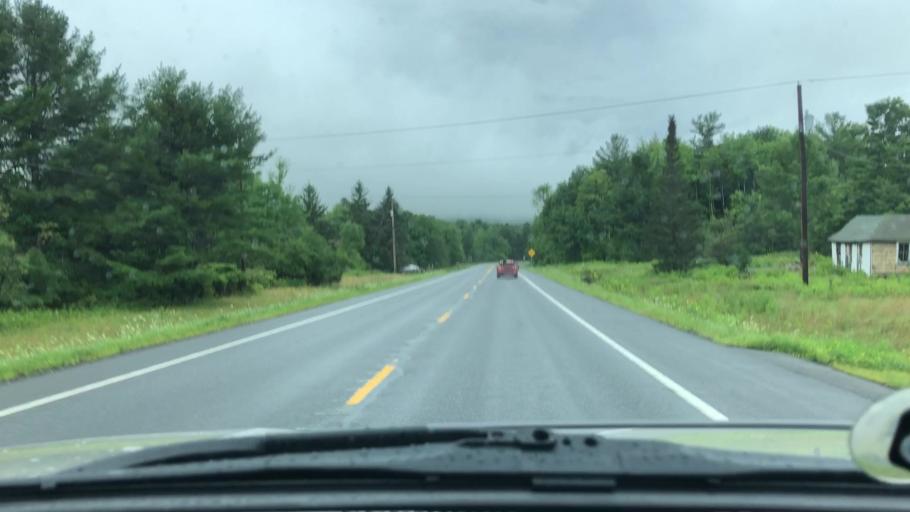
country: US
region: New York
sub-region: Greene County
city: Cairo
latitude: 42.3230
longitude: -74.1769
